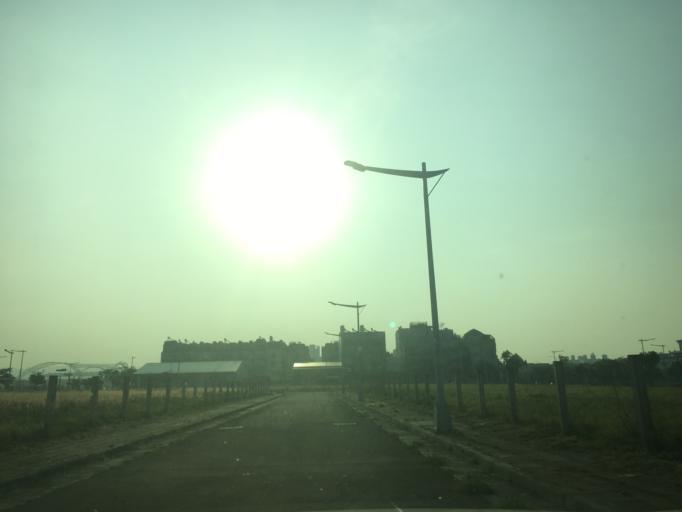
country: TW
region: Taiwan
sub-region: Taichung City
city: Taichung
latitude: 24.1958
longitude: 120.6744
